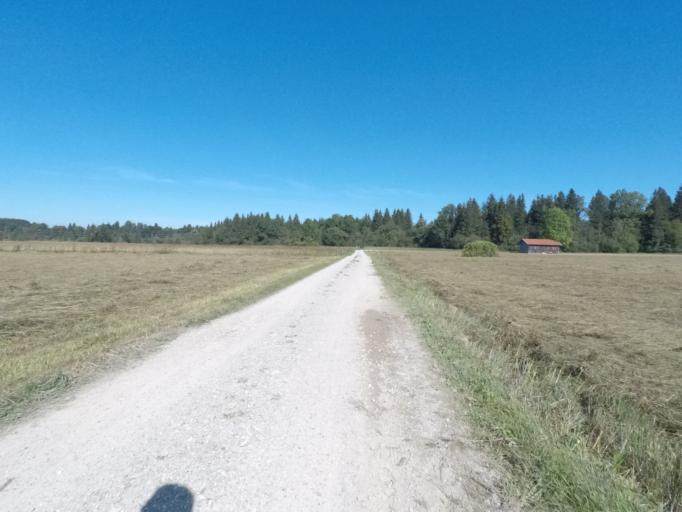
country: DE
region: Bavaria
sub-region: Upper Bavaria
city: Greiling
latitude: 47.7476
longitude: 11.6109
